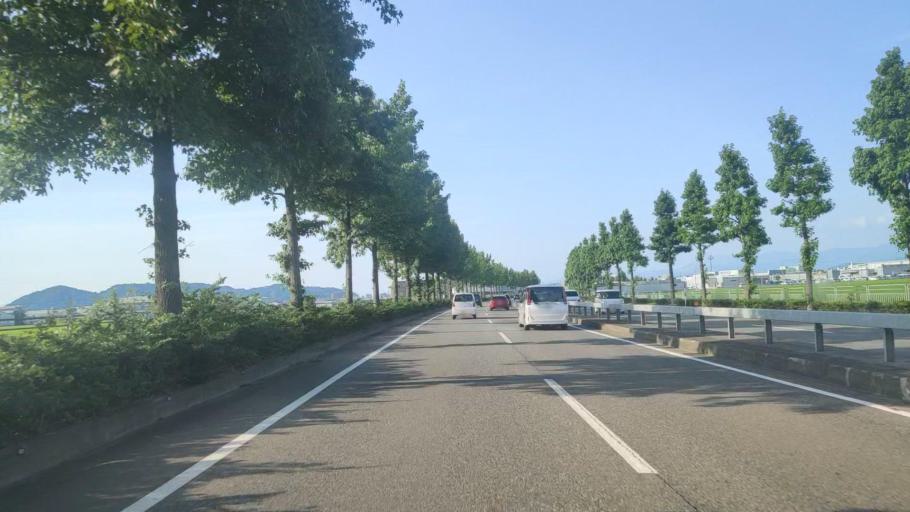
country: JP
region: Fukui
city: Fukui-shi
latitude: 36.0152
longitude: 136.2099
